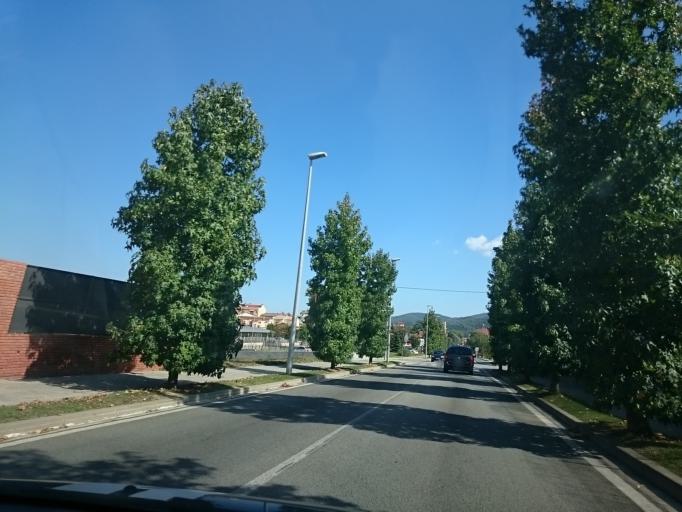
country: ES
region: Catalonia
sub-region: Provincia de Barcelona
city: Llinars del Valles
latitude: 41.6402
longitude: 2.3906
